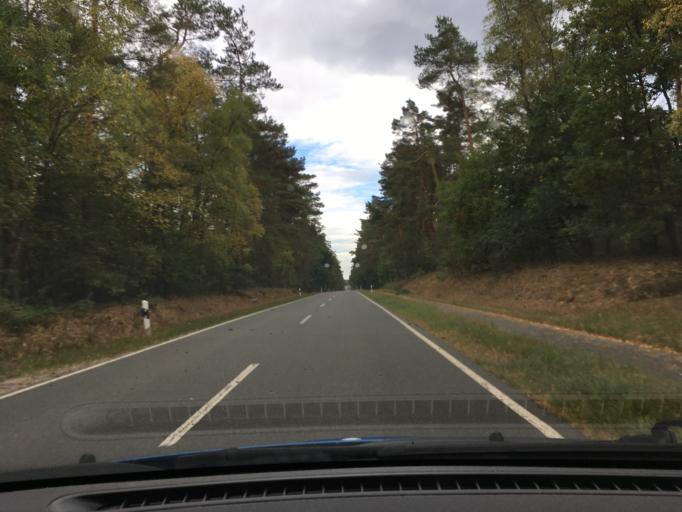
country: DE
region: Lower Saxony
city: Jesteburg
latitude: 53.2589
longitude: 9.9125
